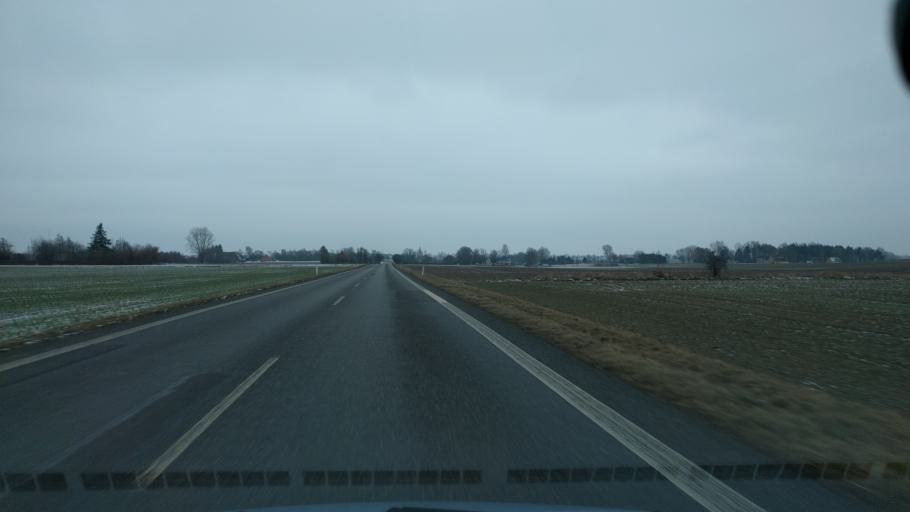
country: DK
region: Zealand
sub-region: Guldborgsund Kommune
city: Stubbekobing
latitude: 54.8254
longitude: 11.9948
